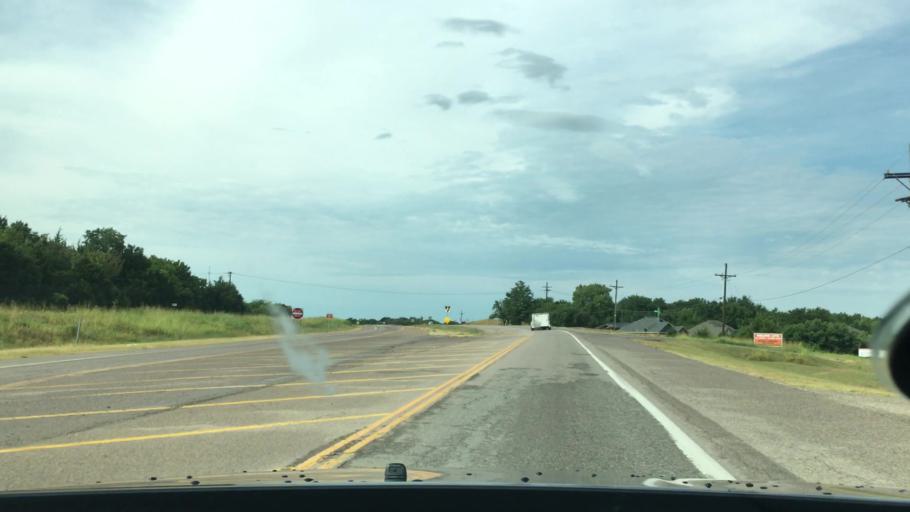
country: US
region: Oklahoma
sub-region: Pontotoc County
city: Ada
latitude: 34.7455
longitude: -96.7061
